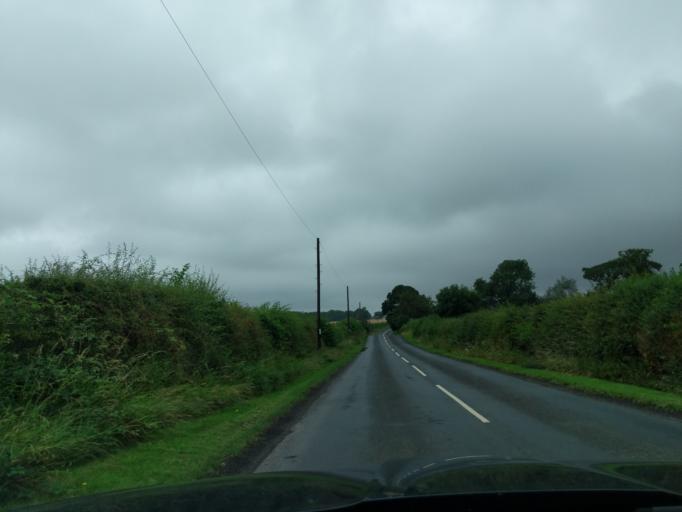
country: GB
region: England
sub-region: Northumberland
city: Ford
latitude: 55.6695
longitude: -2.1020
